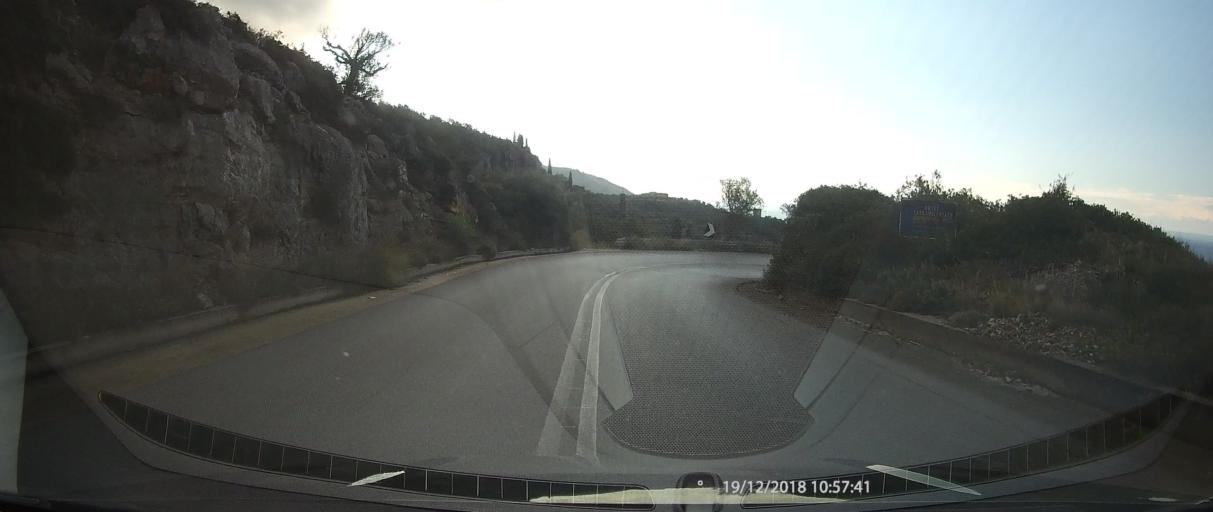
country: GR
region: Peloponnese
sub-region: Nomos Messinias
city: Kardamyli
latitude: 36.8961
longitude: 22.2370
